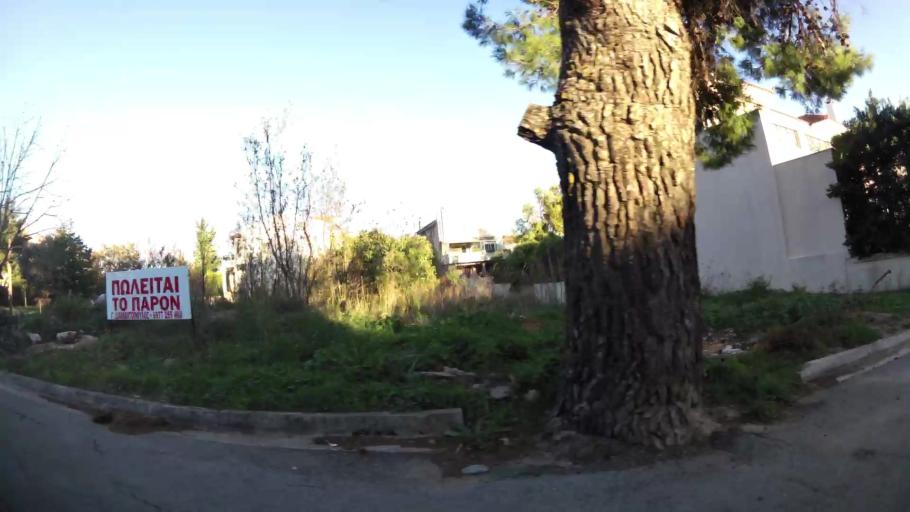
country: GR
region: Attica
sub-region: Nomarchia Anatolikis Attikis
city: Kryoneri
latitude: 38.1341
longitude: 23.8247
